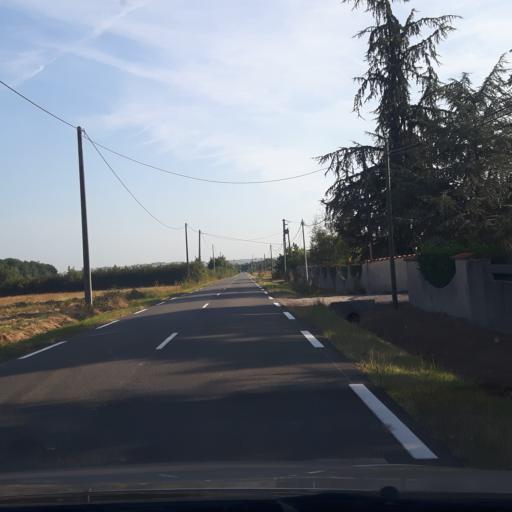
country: FR
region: Midi-Pyrenees
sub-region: Departement de la Haute-Garonne
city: Montjoire
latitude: 43.7732
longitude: 1.5493
